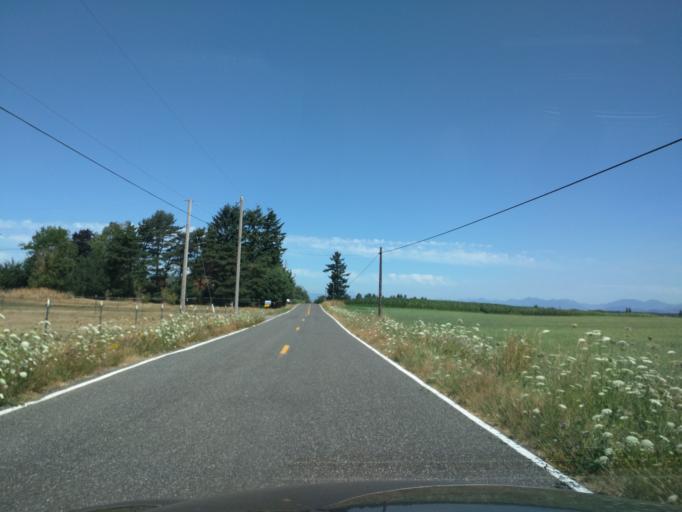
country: US
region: Washington
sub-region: Whatcom County
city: Lynden
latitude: 48.8830
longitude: -122.4146
